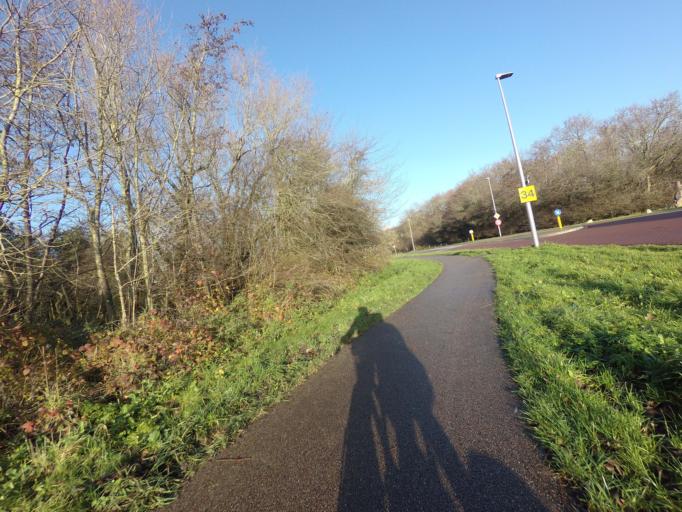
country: NL
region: North Holland
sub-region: Gemeente Texel
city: Den Burg
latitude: 53.1513
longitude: 4.8653
